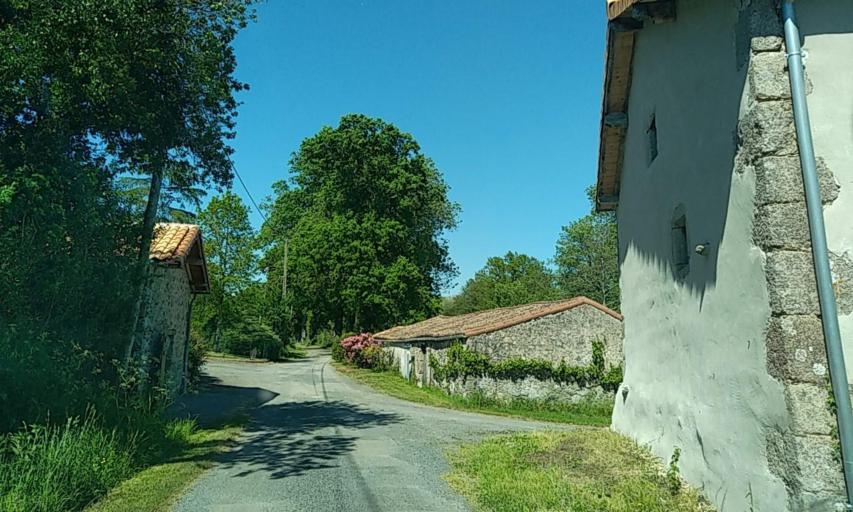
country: FR
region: Poitou-Charentes
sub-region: Departement des Deux-Sevres
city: Boisme
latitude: 46.7667
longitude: -0.4456
